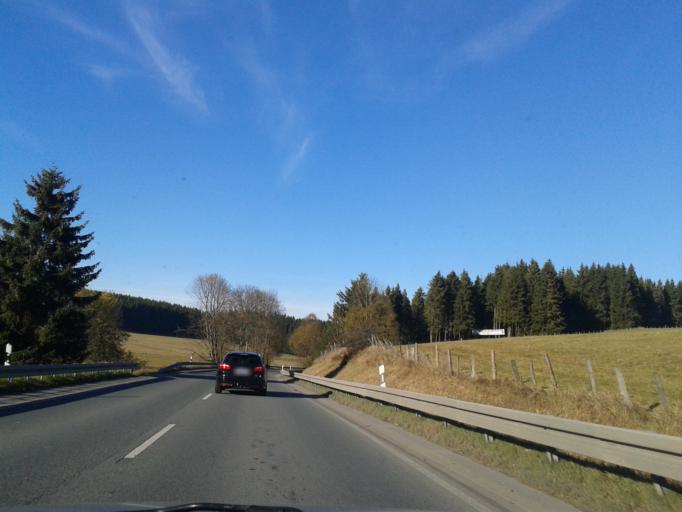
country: DE
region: North Rhine-Westphalia
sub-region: Regierungsbezirk Arnsberg
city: Winterberg
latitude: 51.2126
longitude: 8.5375
